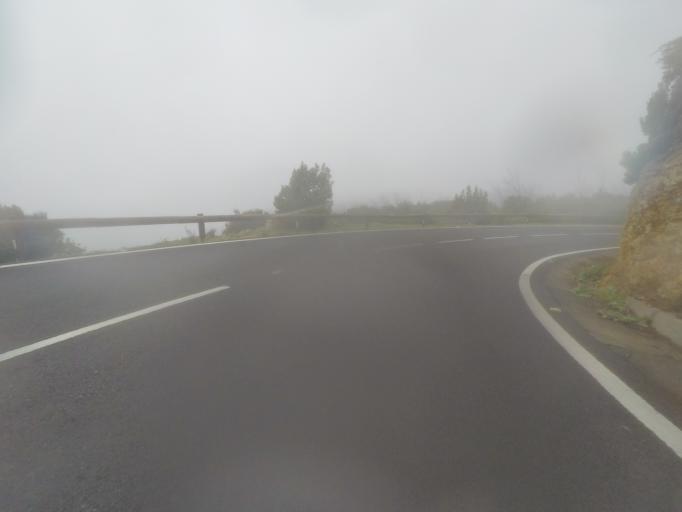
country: ES
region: Canary Islands
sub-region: Provincia de Santa Cruz de Tenerife
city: Vallehermosa
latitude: 28.1290
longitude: -17.2755
